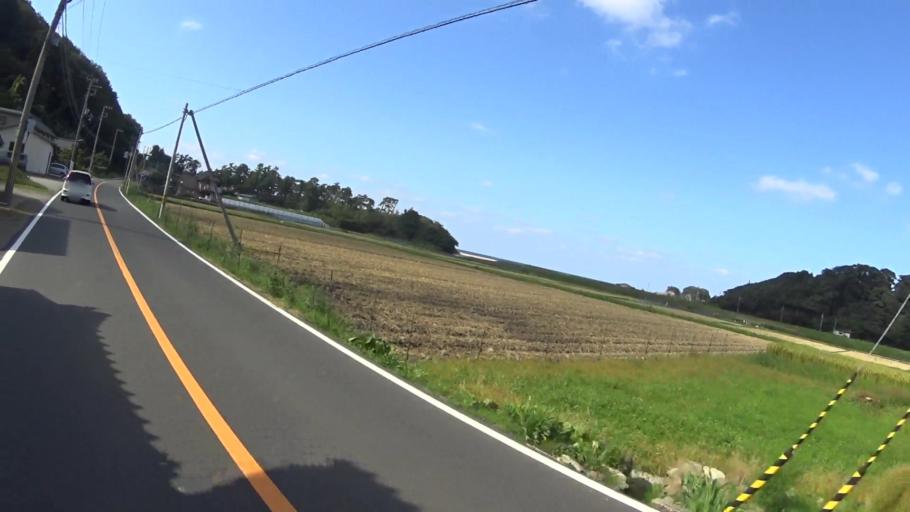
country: JP
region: Kyoto
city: Miyazu
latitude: 35.7483
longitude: 135.1618
